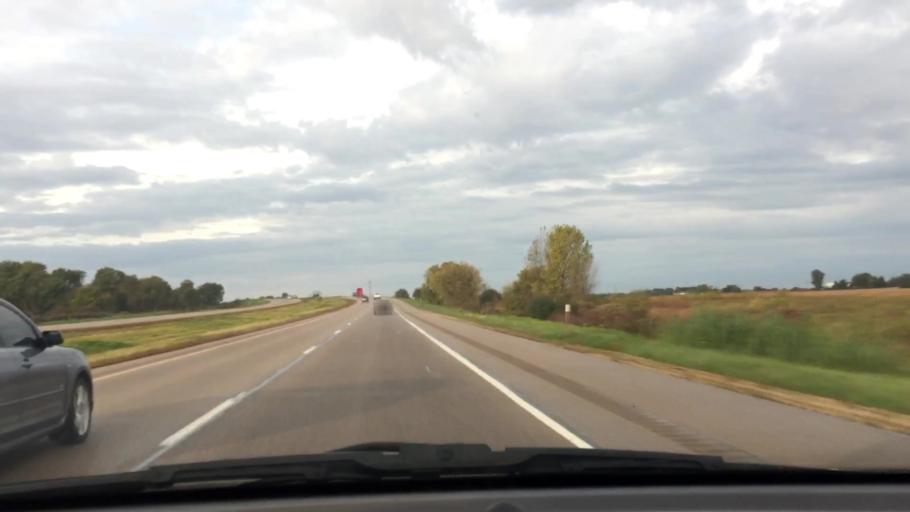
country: US
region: Wisconsin
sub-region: Rock County
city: Clinton
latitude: 42.5790
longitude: -88.7891
